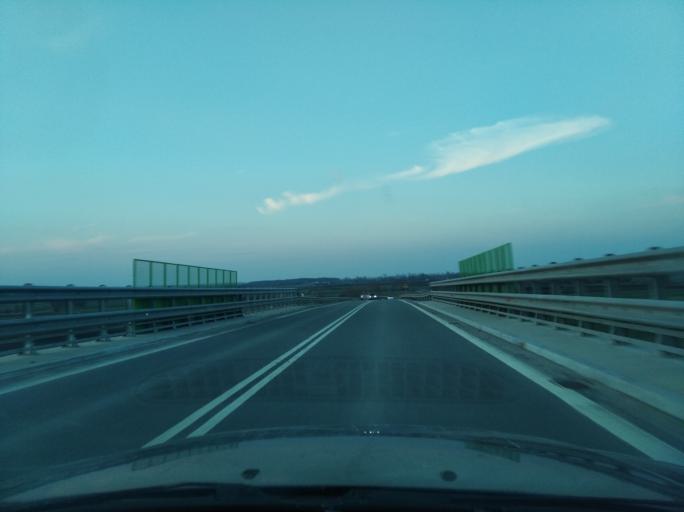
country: PL
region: Subcarpathian Voivodeship
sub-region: Powiat przeworski
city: Grzeska
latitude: 50.0757
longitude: 22.4722
